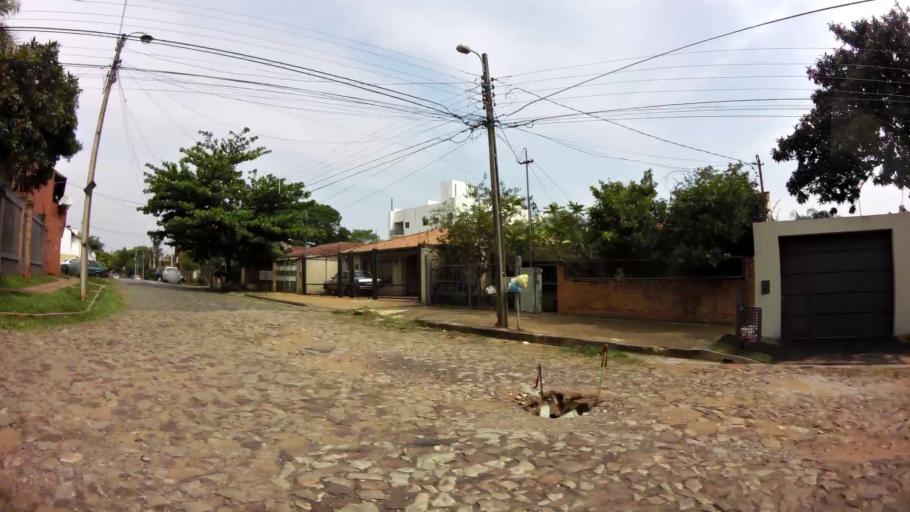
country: PY
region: Asuncion
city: Asuncion
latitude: -25.2733
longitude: -57.5688
